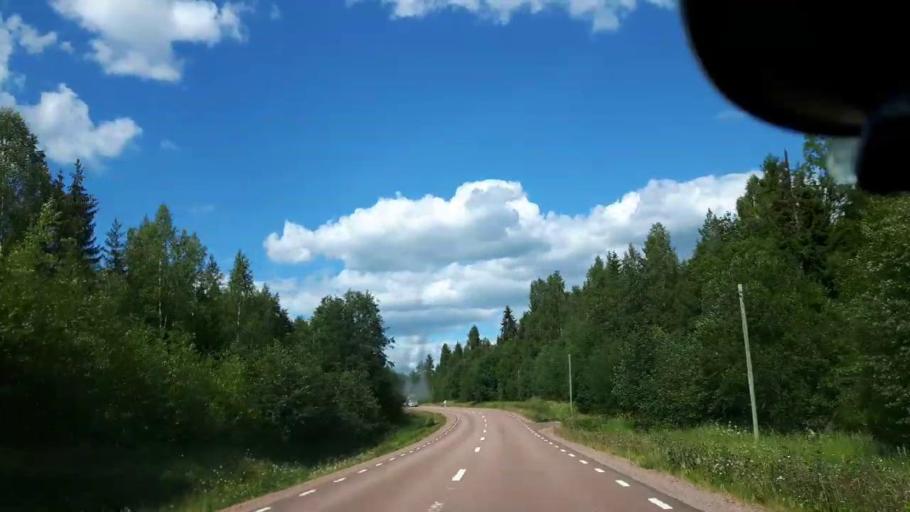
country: SE
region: Jaemtland
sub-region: Ragunda Kommun
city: Hammarstrand
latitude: 63.0306
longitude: 16.5226
